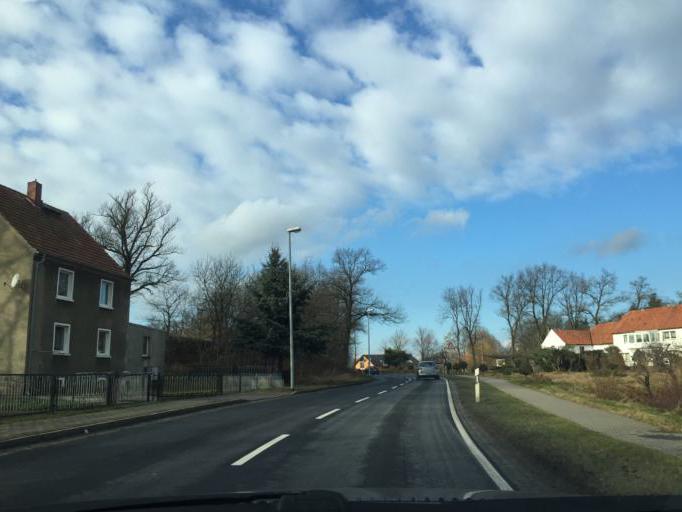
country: DE
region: Saxony
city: Radeburg
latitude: 51.2036
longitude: 13.7669
